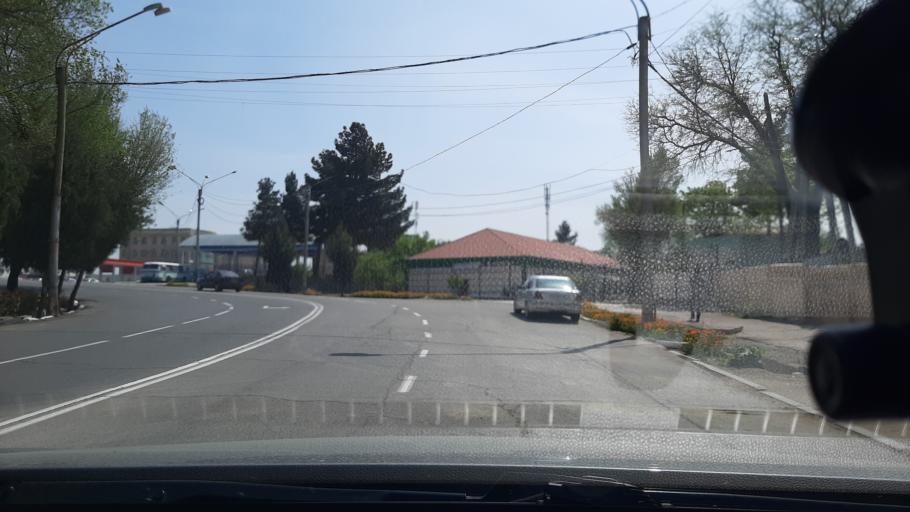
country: TJ
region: Viloyati Sughd
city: Khujand
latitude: 40.2924
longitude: 69.6393
